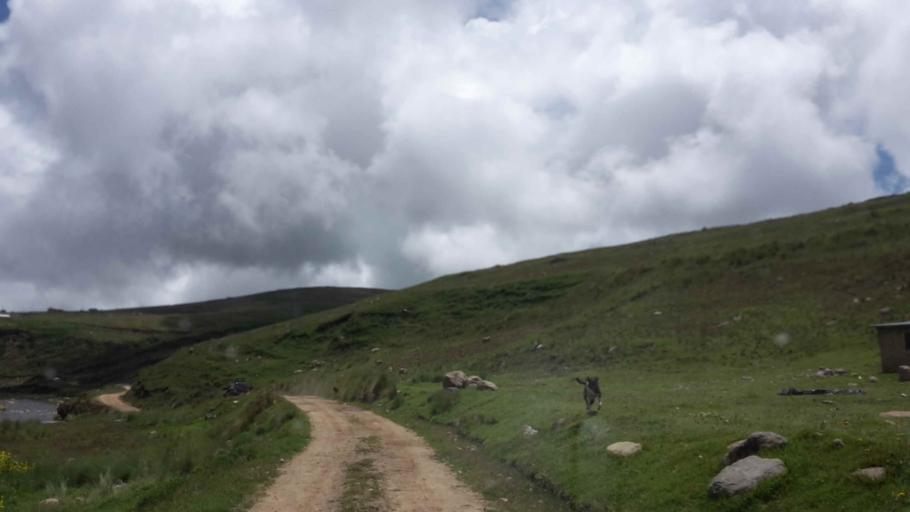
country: BO
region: Cochabamba
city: Cochabamba
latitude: -17.1844
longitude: -66.0656
